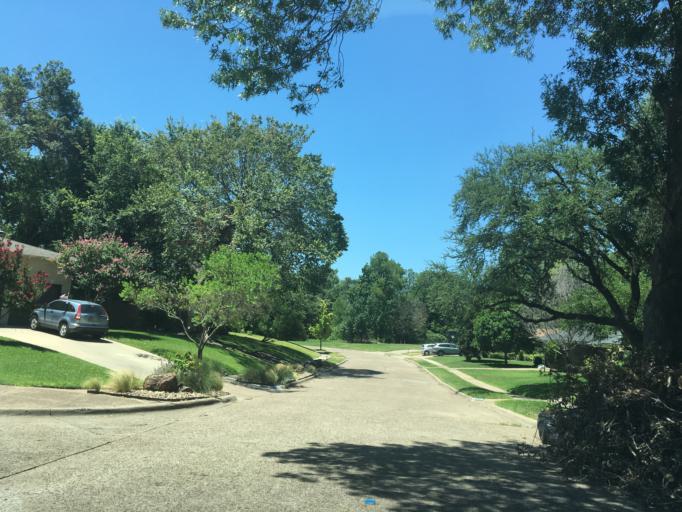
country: US
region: Texas
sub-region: Dallas County
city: Highland Park
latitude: 32.8477
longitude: -96.7079
